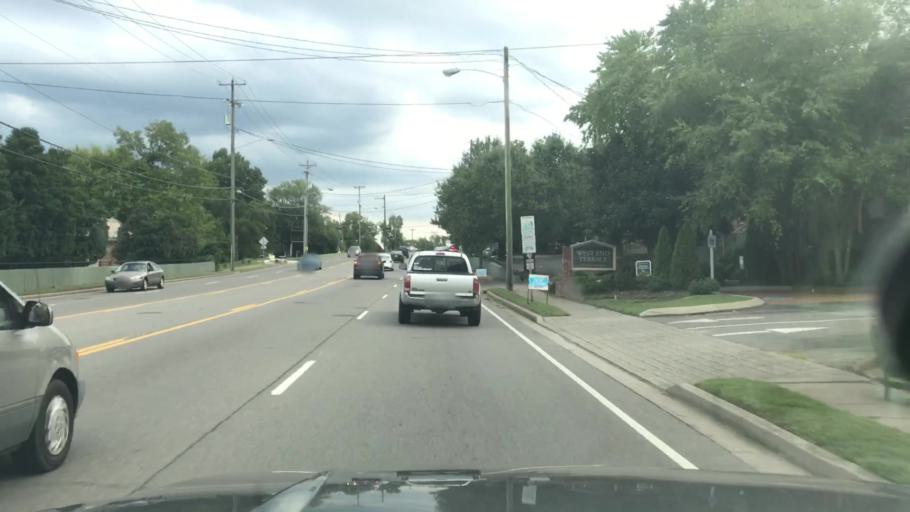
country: US
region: Tennessee
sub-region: Davidson County
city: Belle Meade
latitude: 36.1431
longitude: -86.8578
